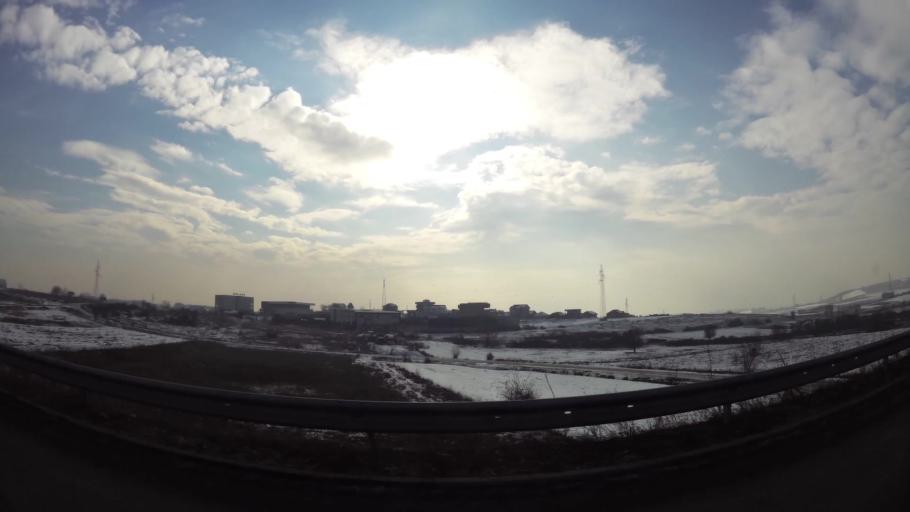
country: MK
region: Suto Orizari
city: Suto Orizare
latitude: 42.0515
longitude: 21.4269
